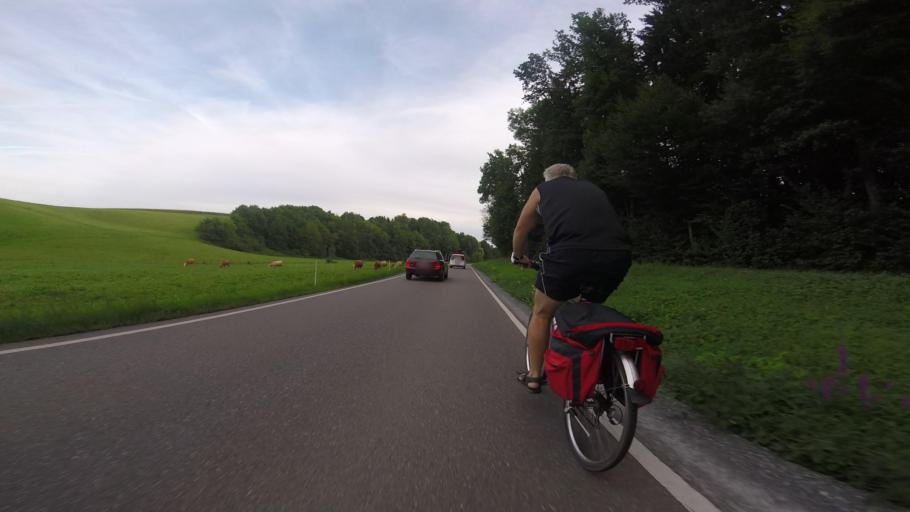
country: DE
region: Baden-Wuerttemberg
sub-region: Regierungsbezirk Stuttgart
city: Aspach
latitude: 48.9837
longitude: 9.3960
